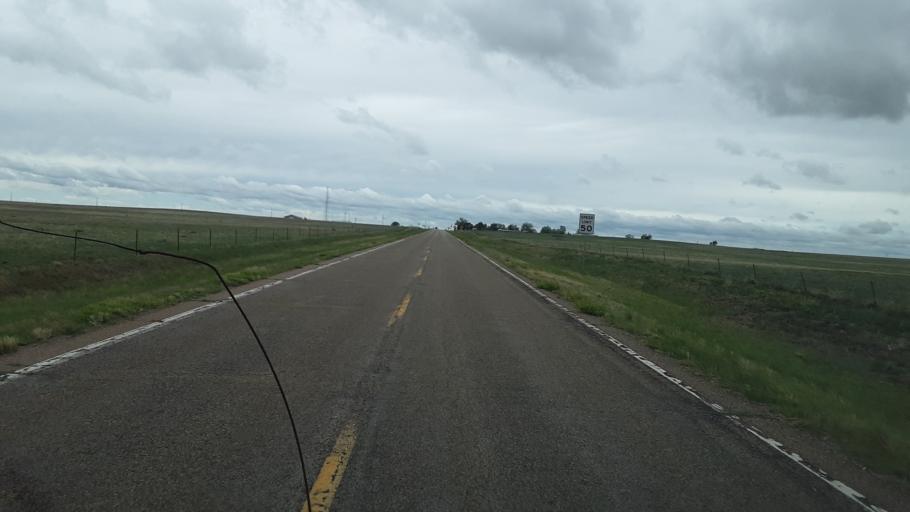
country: US
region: Colorado
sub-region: Lincoln County
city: Hugo
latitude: 38.8519
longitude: -103.6922
